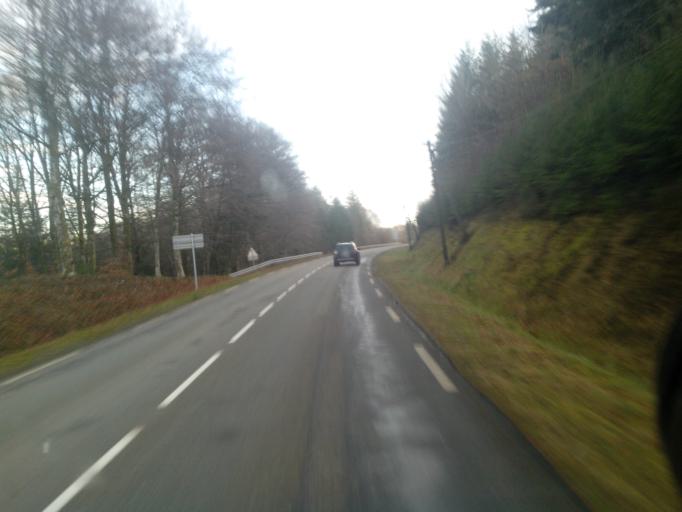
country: FR
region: Limousin
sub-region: Departement de la Correze
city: Meymac
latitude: 45.5797
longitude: 2.1317
